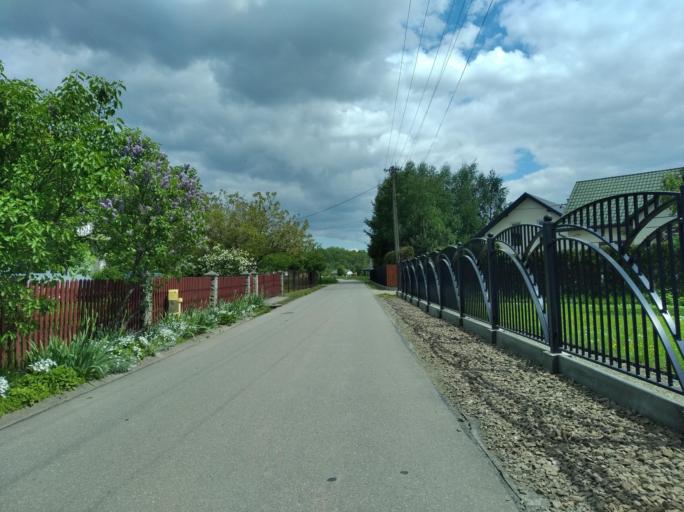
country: PL
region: Subcarpathian Voivodeship
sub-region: Powiat brzozowski
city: Jasionow
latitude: 49.6622
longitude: 21.9880
